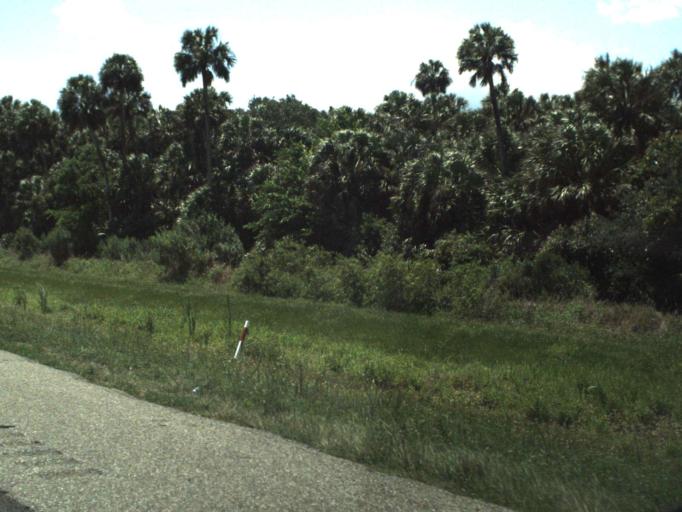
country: US
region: Florida
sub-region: Volusia County
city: DeBary
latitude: 28.8513
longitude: -81.3036
